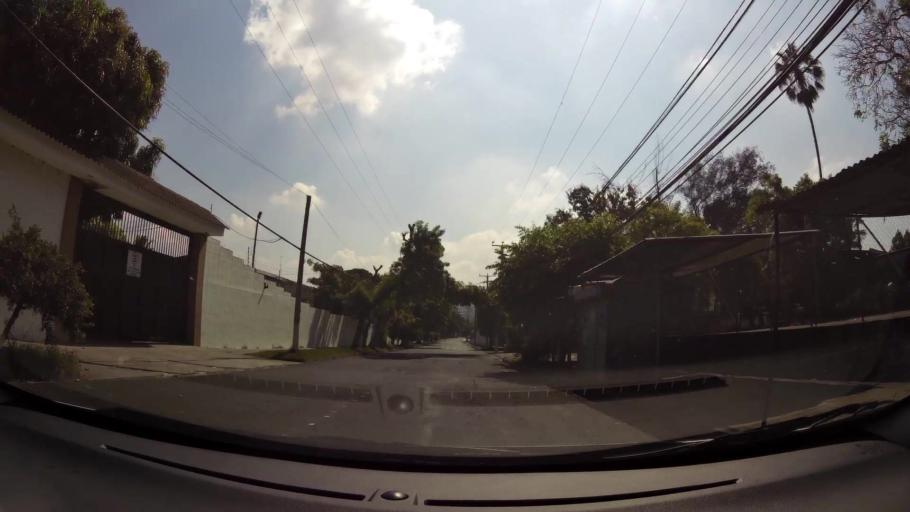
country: SV
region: La Libertad
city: Antiguo Cuscatlan
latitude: 13.6887
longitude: -89.2312
